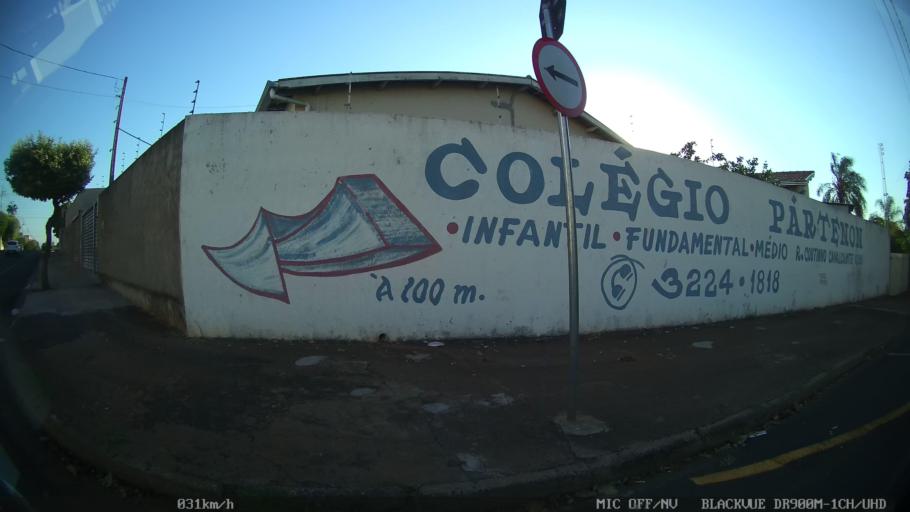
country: BR
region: Sao Paulo
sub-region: Sao Jose Do Rio Preto
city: Sao Jose do Rio Preto
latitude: -20.7891
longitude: -49.3618
